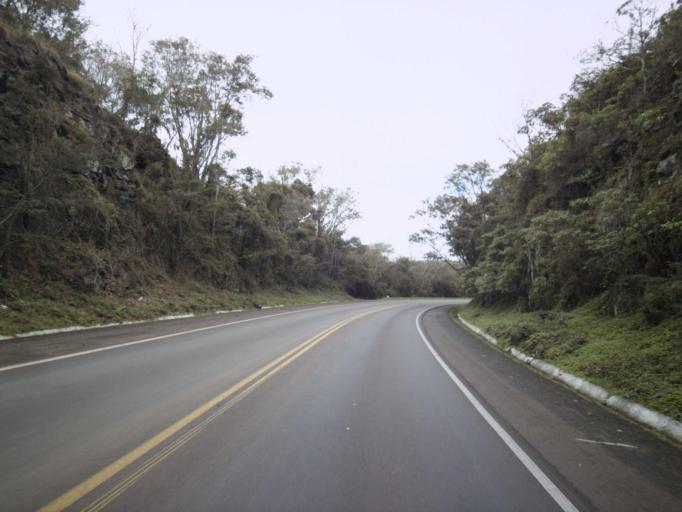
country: BR
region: Santa Catarina
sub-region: Concordia
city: Concordia
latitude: -27.3587
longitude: -51.9878
